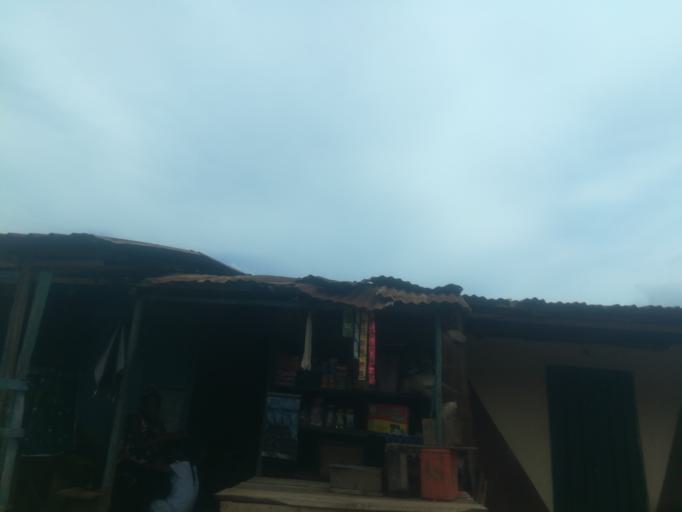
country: NG
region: Oyo
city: Ibadan
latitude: 7.3749
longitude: 3.9536
